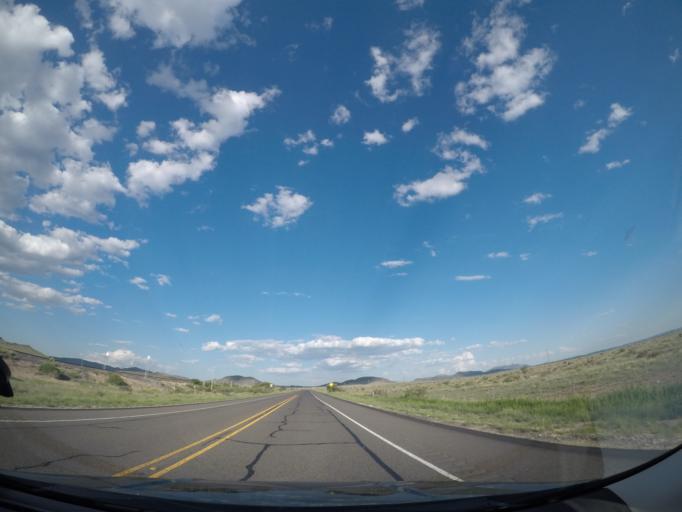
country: US
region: Texas
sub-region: Presidio County
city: Marfa
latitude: 30.2708
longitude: -103.8378
